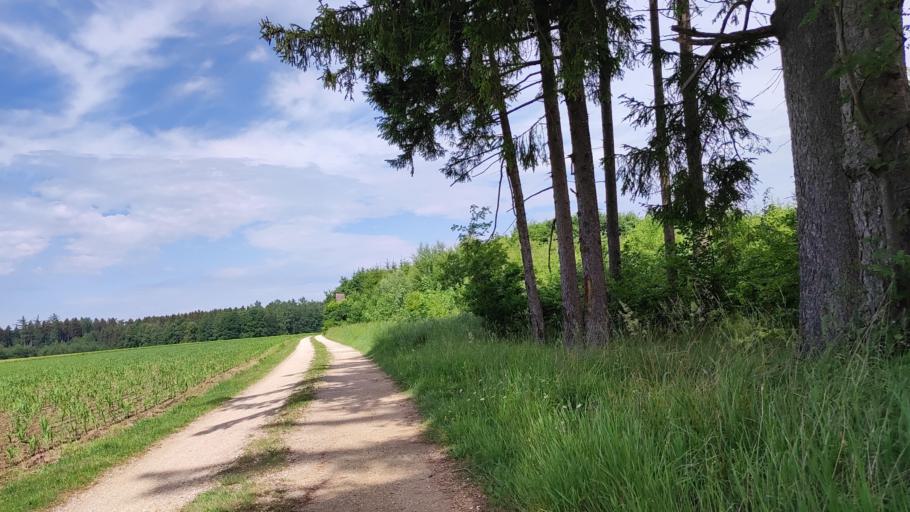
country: DE
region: Bavaria
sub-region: Swabia
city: Landensberg
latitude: 48.4310
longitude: 10.5387
